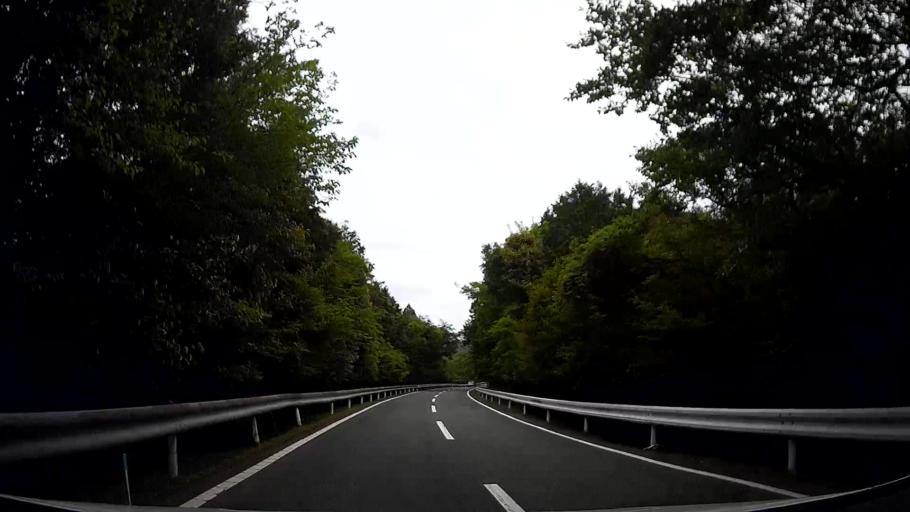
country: JP
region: Shizuoka
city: Ito
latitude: 34.9065
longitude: 139.0628
